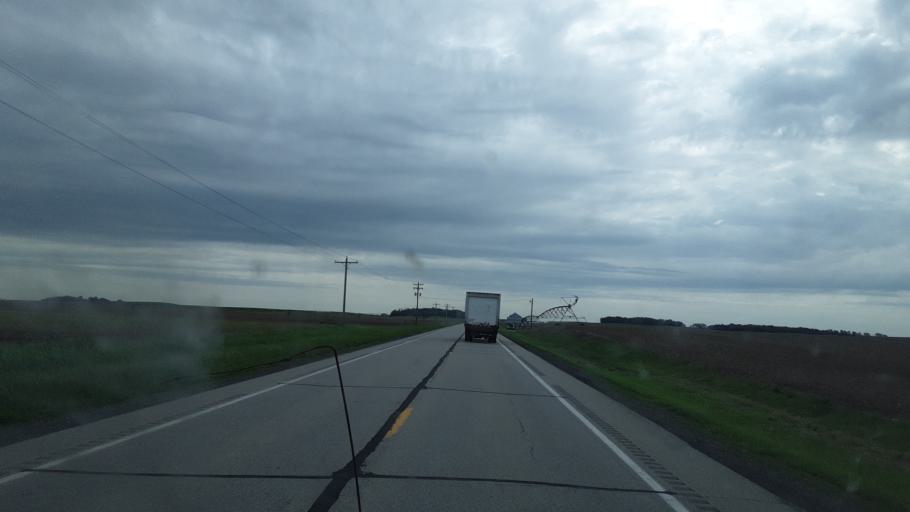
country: US
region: Illinois
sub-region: Mason County
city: Manito
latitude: 40.3032
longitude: -89.8024
